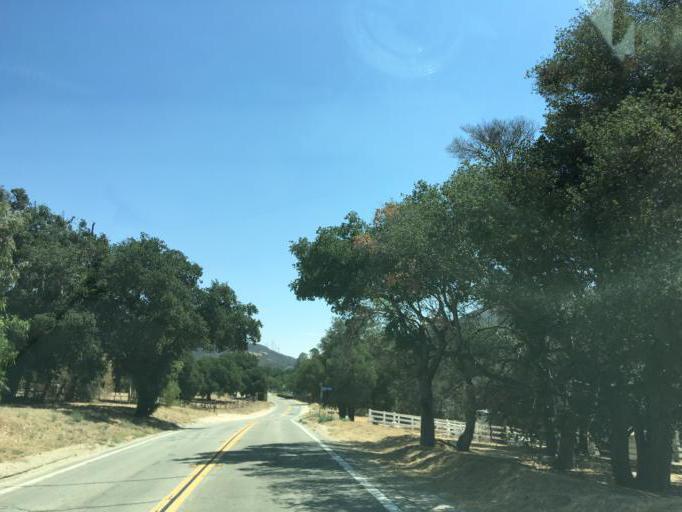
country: US
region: California
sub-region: Los Angeles County
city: Green Valley
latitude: 34.6200
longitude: -118.4171
